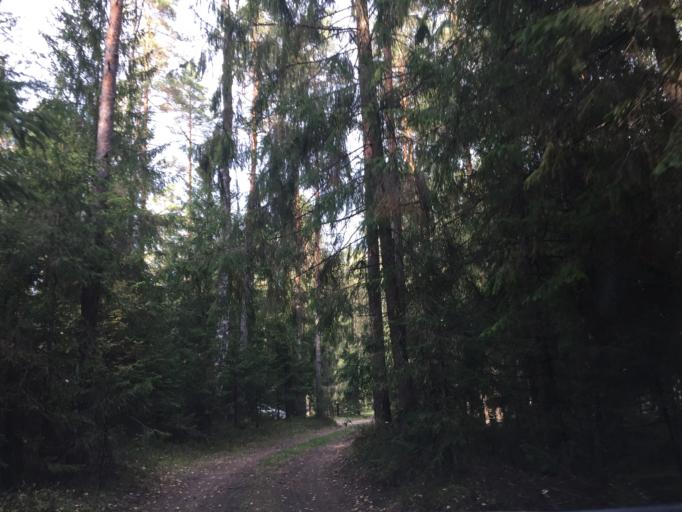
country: LV
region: Baldone
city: Baldone
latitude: 56.7846
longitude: 24.4411
